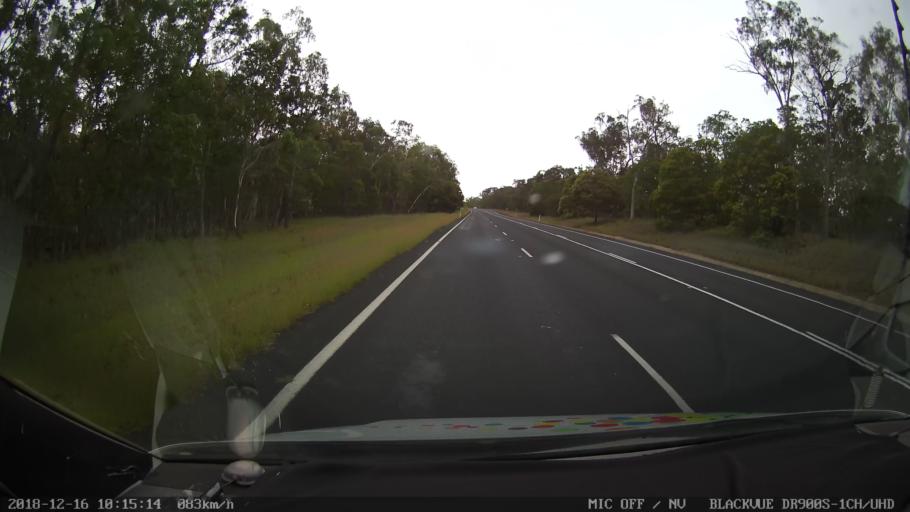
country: AU
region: New South Wales
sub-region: Tenterfield Municipality
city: Carrolls Creek
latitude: -29.2793
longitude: 151.9708
